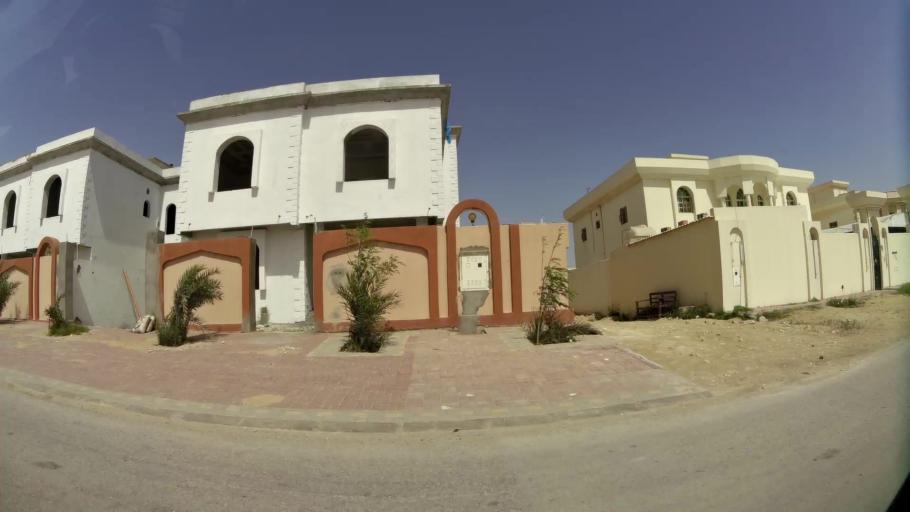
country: QA
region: Baladiyat Umm Salal
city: Umm Salal Muhammad
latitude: 25.3771
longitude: 51.4163
